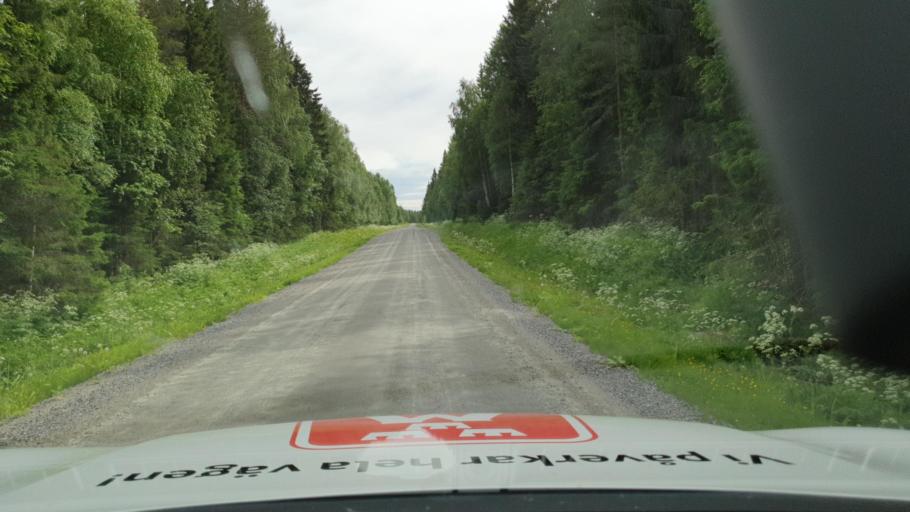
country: SE
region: Vaesterbotten
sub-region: Skelleftea Kommun
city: Burea
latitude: 64.4336
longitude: 21.0152
